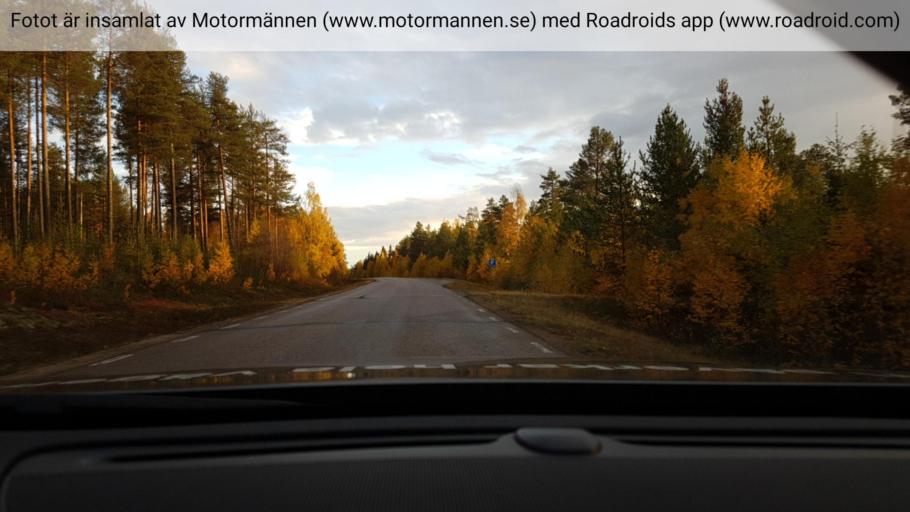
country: SE
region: Norrbotten
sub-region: Overkalix Kommun
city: OEverkalix
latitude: 66.6438
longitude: 22.7214
